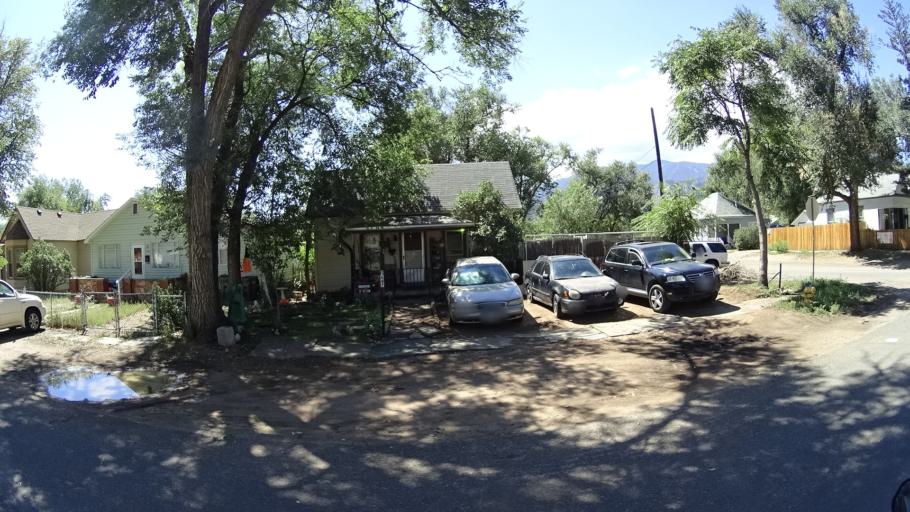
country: US
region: Colorado
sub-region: El Paso County
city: Colorado Springs
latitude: 38.8390
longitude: -104.8526
